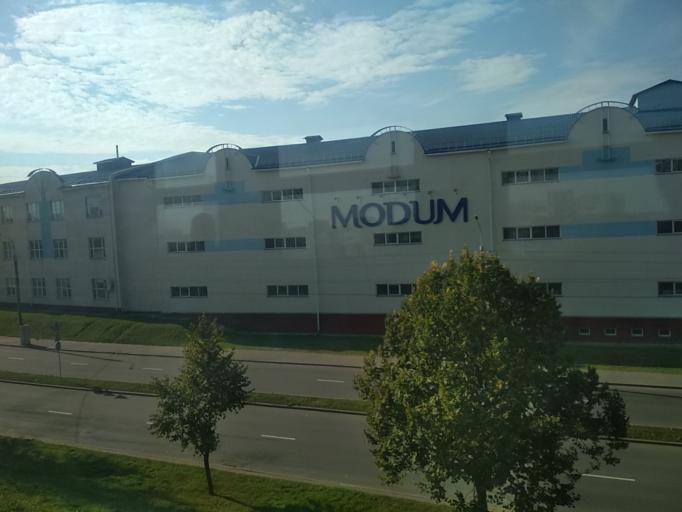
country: BY
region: Minsk
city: Minsk
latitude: 53.8827
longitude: 27.5635
